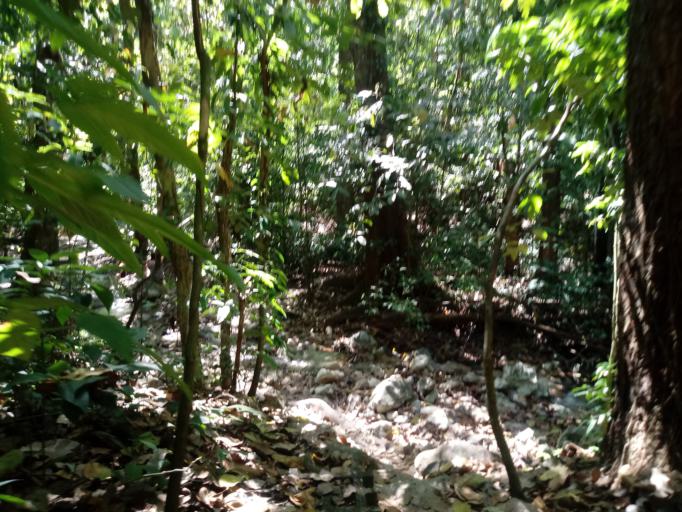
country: CR
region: Puntarenas
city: Paquera
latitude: 9.5846
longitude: -85.1002
